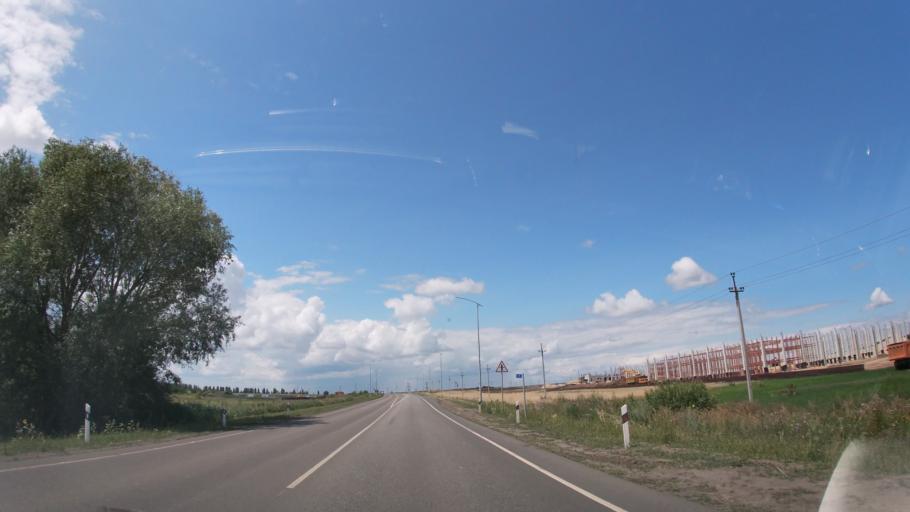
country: RU
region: Belgorod
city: Severnyy
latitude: 50.6672
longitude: 36.5465
